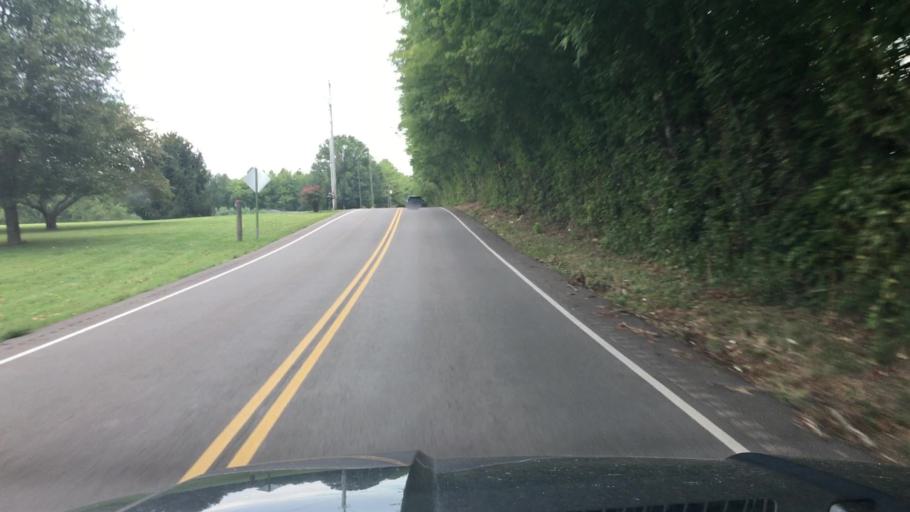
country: US
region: Tennessee
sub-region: Williamson County
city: Thompson's Station
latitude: 35.8073
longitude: -86.8623
